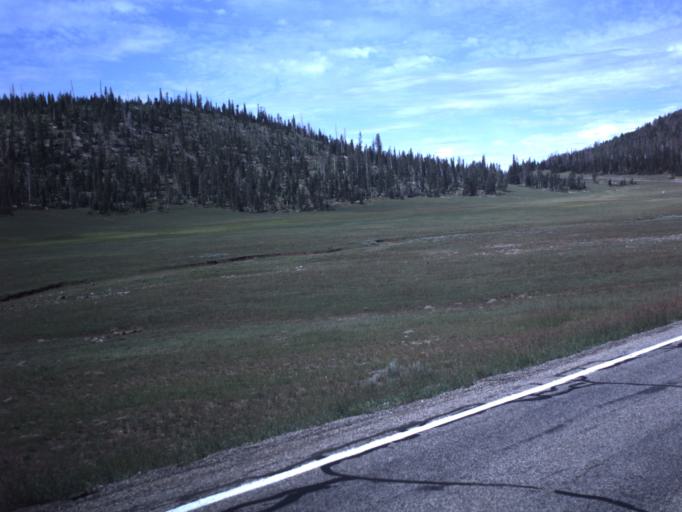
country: US
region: Utah
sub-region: Iron County
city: Cedar City
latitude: 37.5720
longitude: -112.8305
